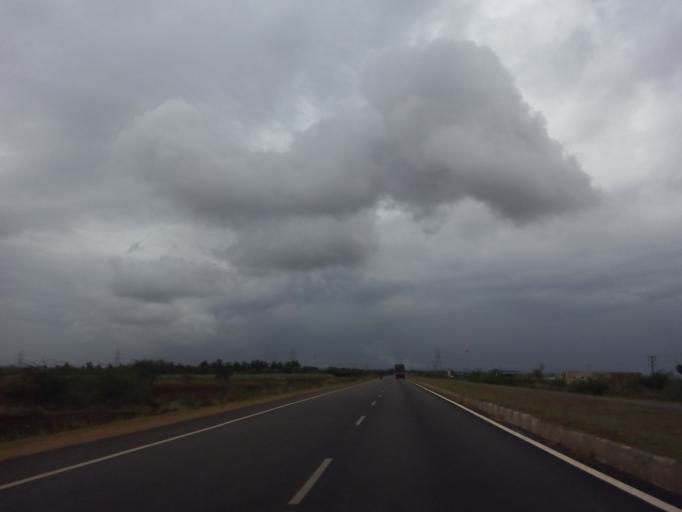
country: IN
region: Karnataka
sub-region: Davanagere
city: Harihar
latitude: 14.5465
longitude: 75.7459
